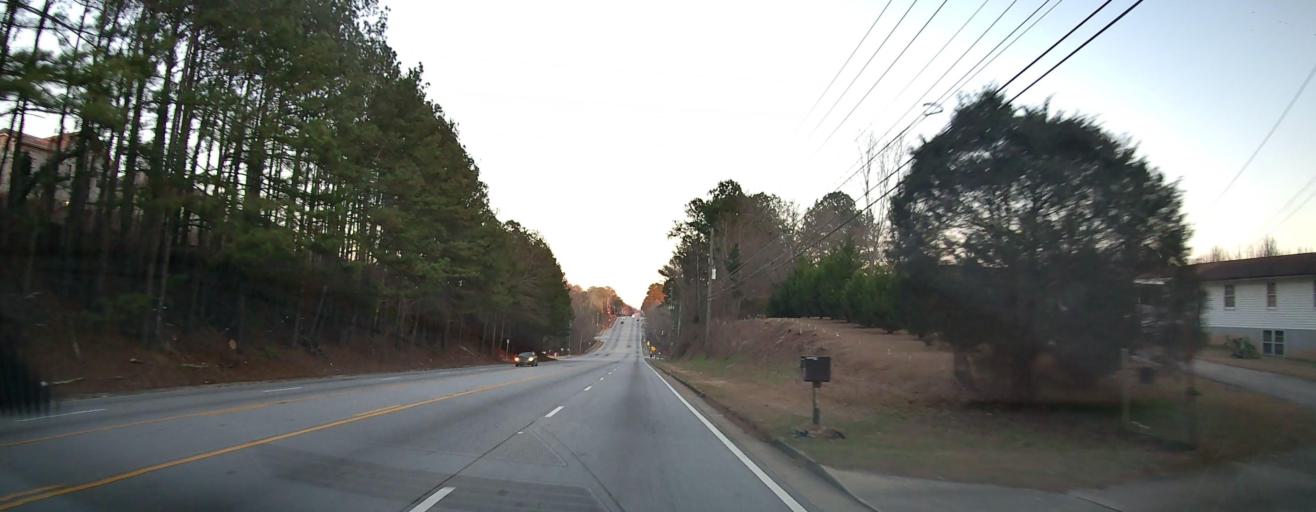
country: US
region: Georgia
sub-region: Clayton County
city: Riverdale
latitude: 33.5508
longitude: -84.4430
